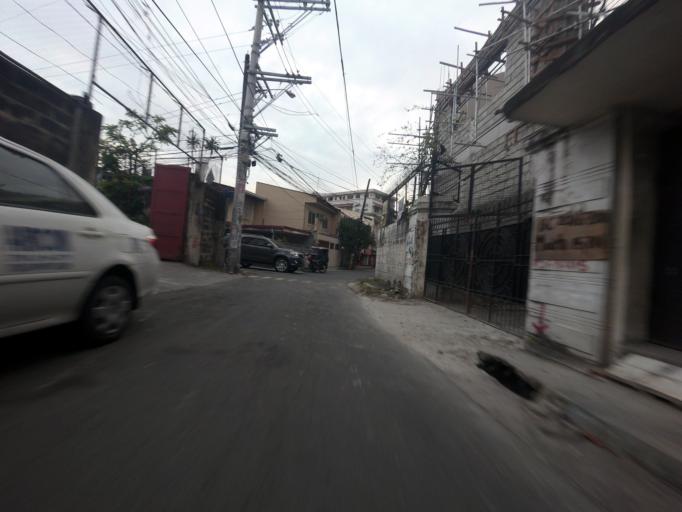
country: PH
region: Metro Manila
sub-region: San Juan
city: San Juan
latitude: 14.6018
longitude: 121.0290
